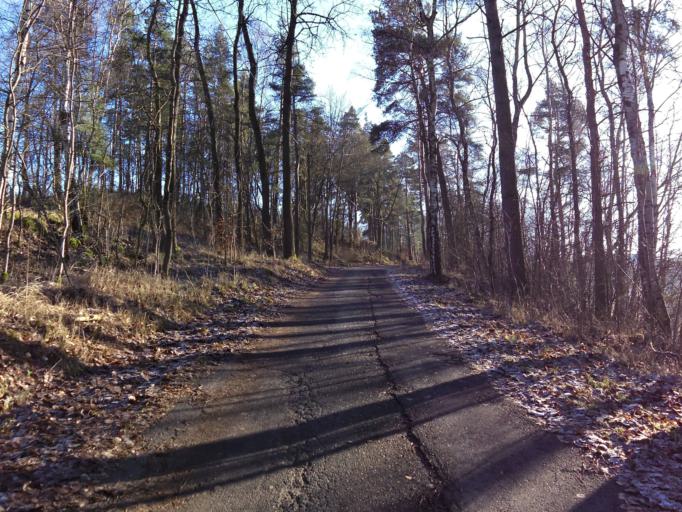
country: DE
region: Bavaria
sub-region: Upper Franconia
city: Roslau
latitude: 50.0830
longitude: 12.0339
